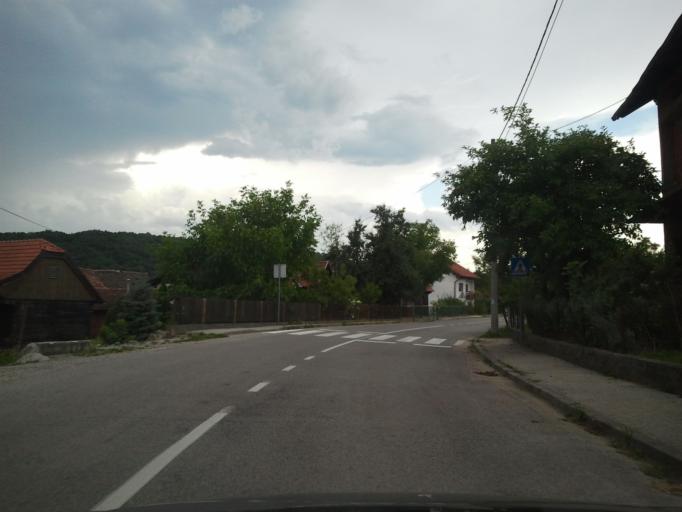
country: HR
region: Sisacko-Moslavacka
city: Glina
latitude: 45.4831
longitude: 15.9989
